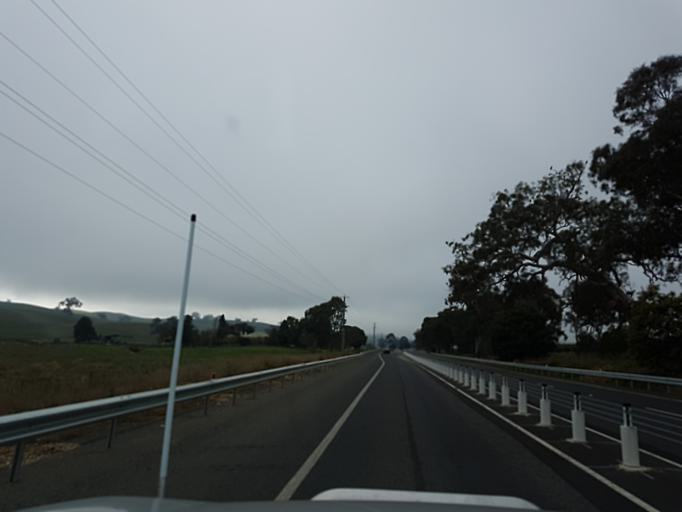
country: AU
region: Victoria
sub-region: Murrindindi
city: Alexandra
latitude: -37.2055
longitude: 145.4605
